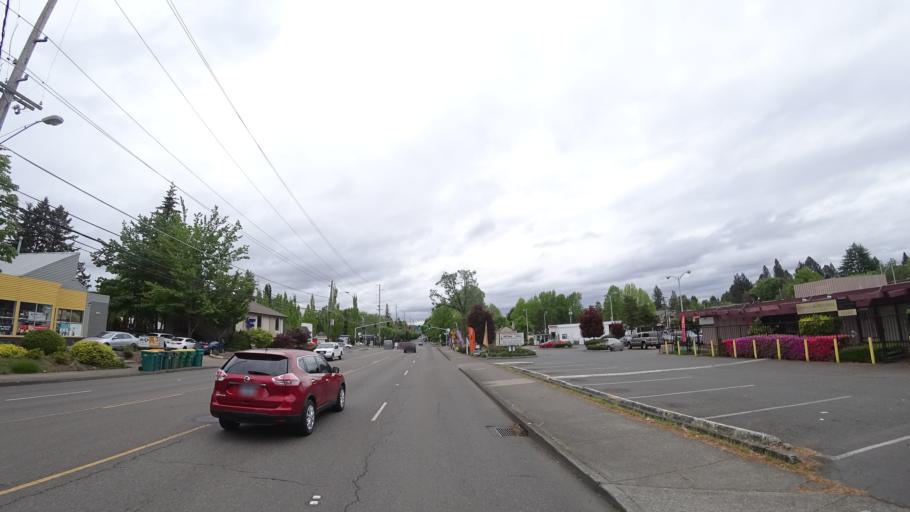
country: US
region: Oregon
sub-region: Washington County
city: Beaverton
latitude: 45.4765
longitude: -122.8017
